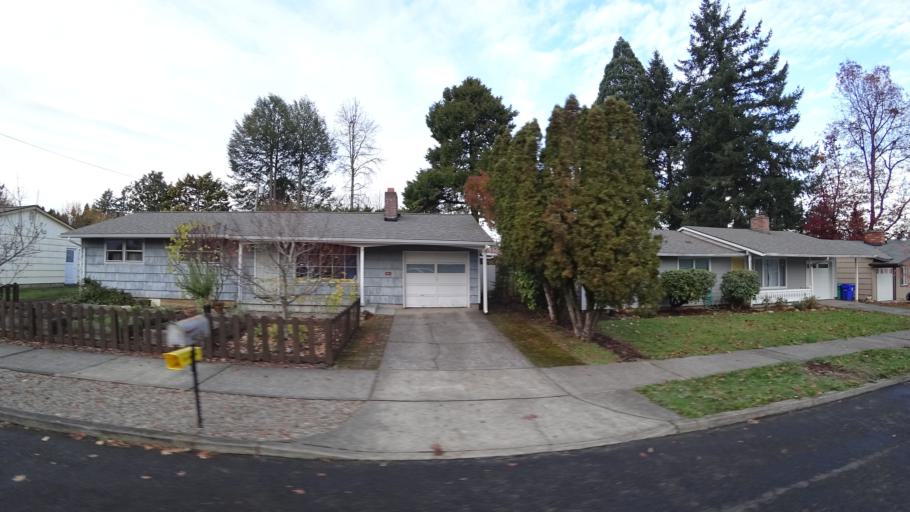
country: US
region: Oregon
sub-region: Multnomah County
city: Lents
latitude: 45.5146
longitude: -122.5169
